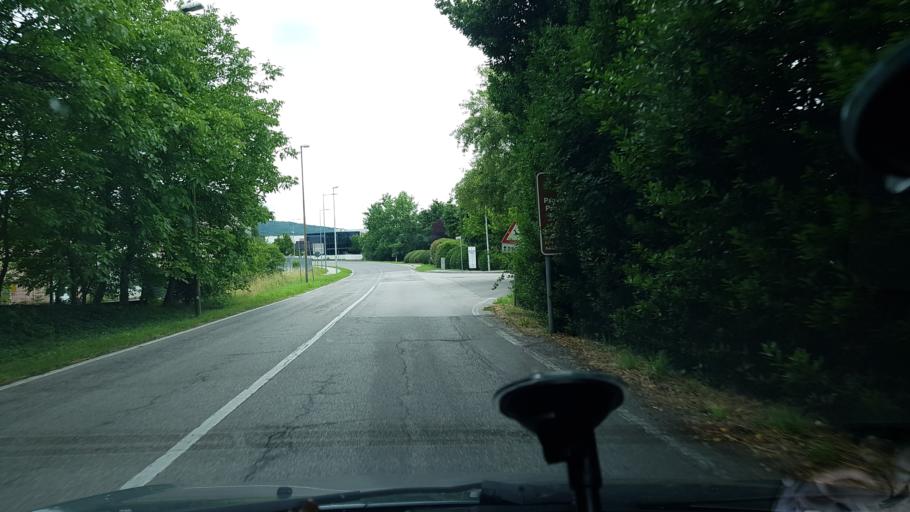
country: IT
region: Friuli Venezia Giulia
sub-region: Provincia di Gorizia
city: Savogna d'Isonzo
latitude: 45.9186
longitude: 13.5991
